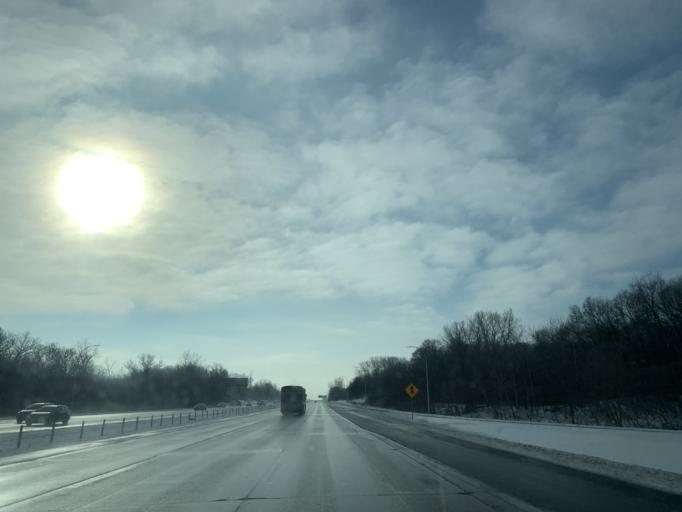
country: US
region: Minnesota
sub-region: Dakota County
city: Apple Valley
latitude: 44.7752
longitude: -93.2175
